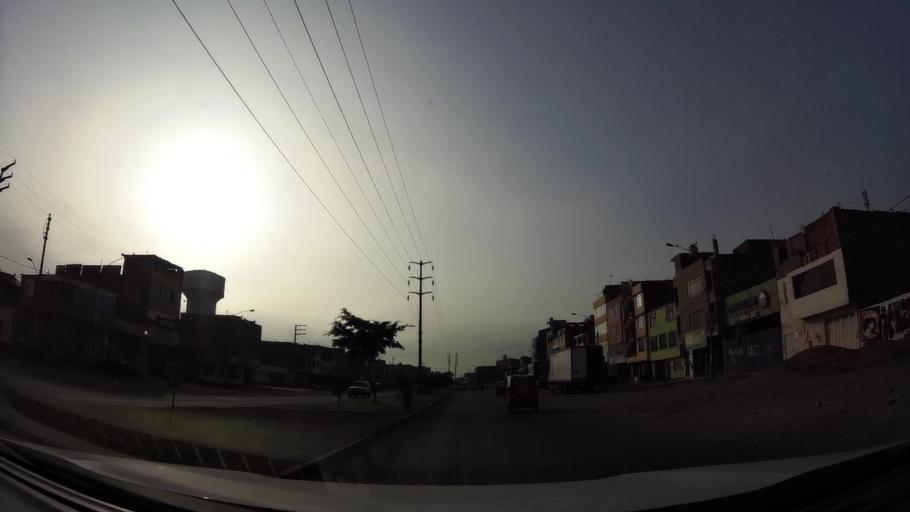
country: PE
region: Lima
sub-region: Lima
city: Independencia
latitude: -12.0013
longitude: -77.1014
